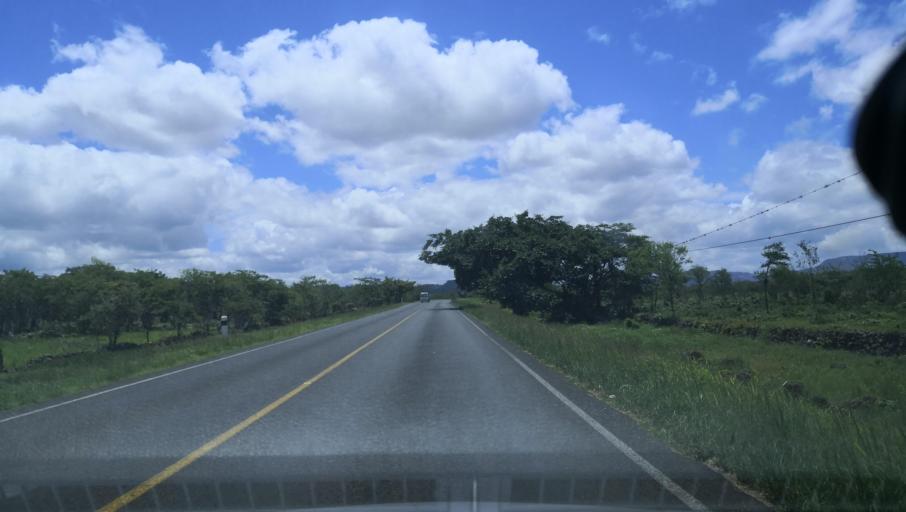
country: NI
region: Esteli
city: Esteli
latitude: 13.2191
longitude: -86.3797
